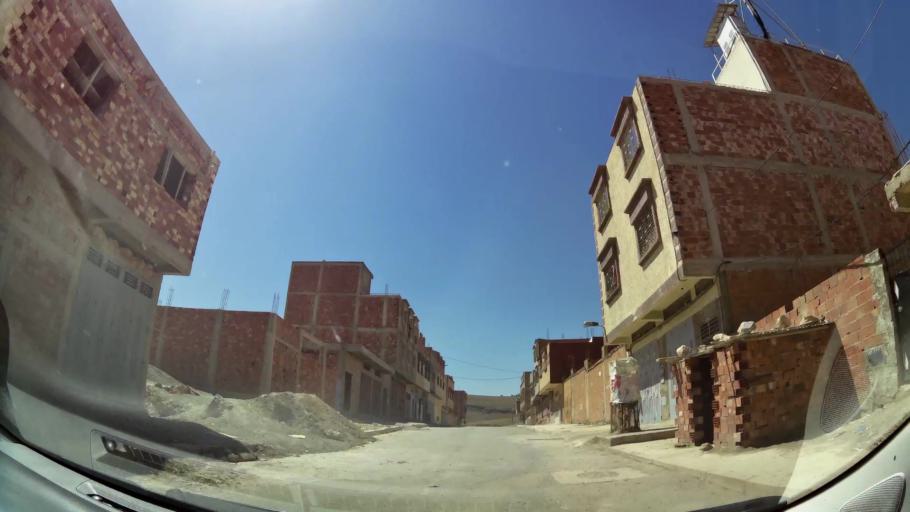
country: MA
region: Oriental
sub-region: Oujda-Angad
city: Oujda
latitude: 34.6492
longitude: -1.8727
